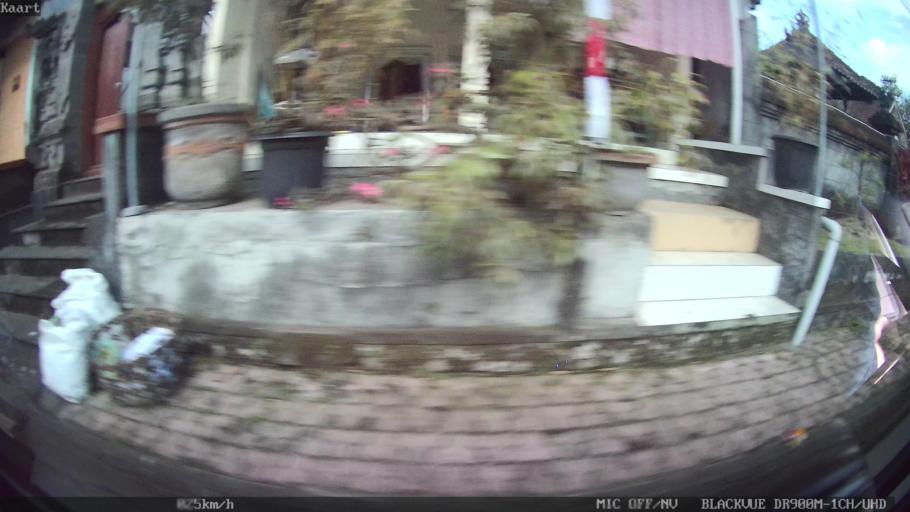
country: ID
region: Bali
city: Banjar Tegal Belodan
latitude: -8.5393
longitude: 115.1220
